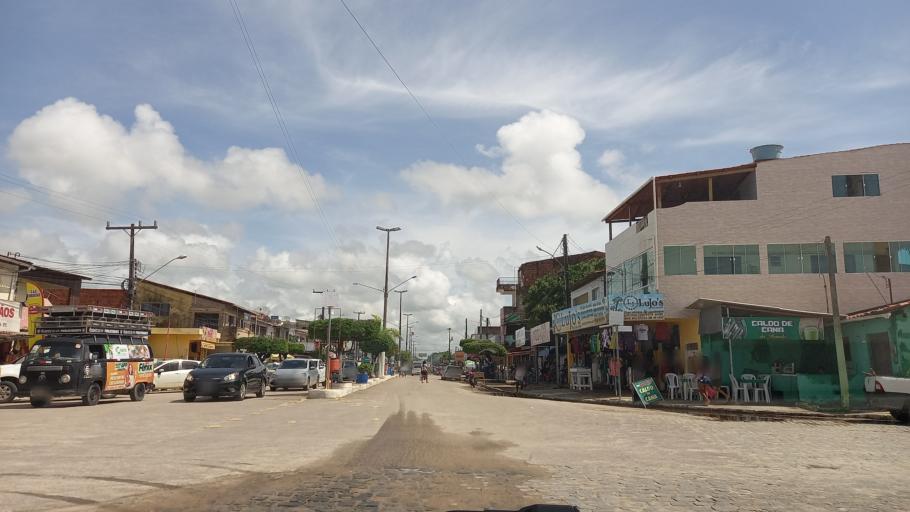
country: BR
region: Pernambuco
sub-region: Sao Jose Da Coroa Grande
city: Sao Jose da Coroa Grande
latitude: -8.8974
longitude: -35.1470
